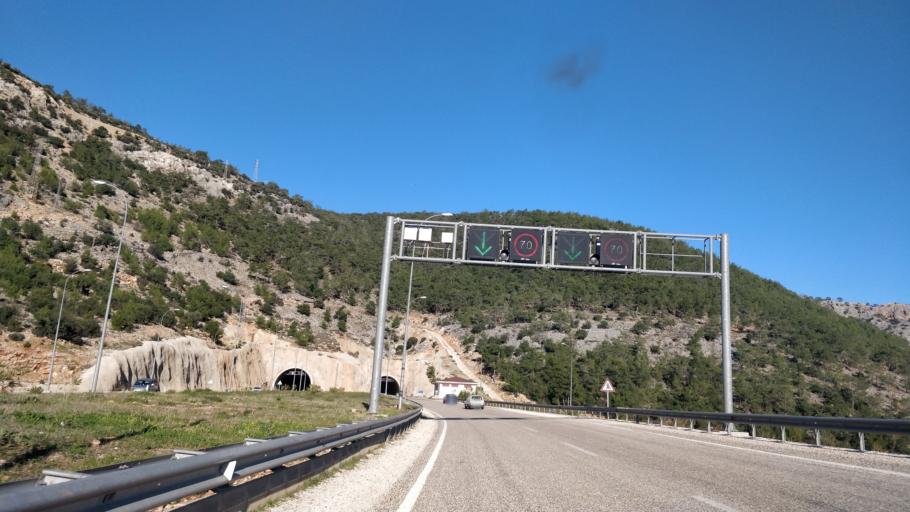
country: TR
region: Mersin
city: Akdere
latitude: 36.2565
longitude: 33.7901
